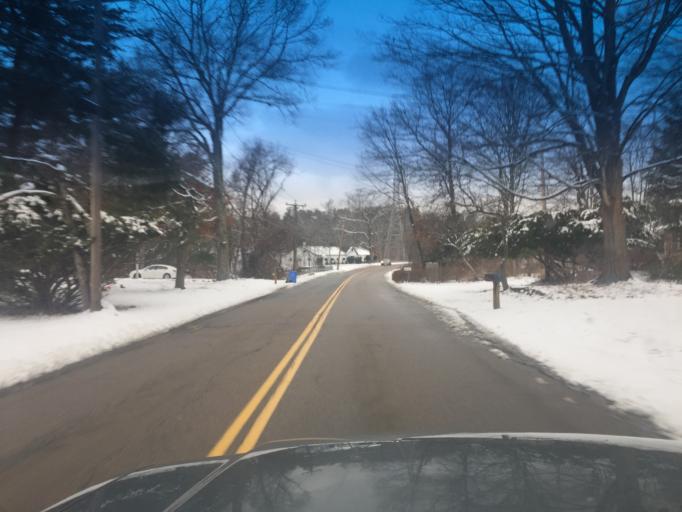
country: US
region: Massachusetts
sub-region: Middlesex County
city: Holliston
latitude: 42.2034
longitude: -71.3981
